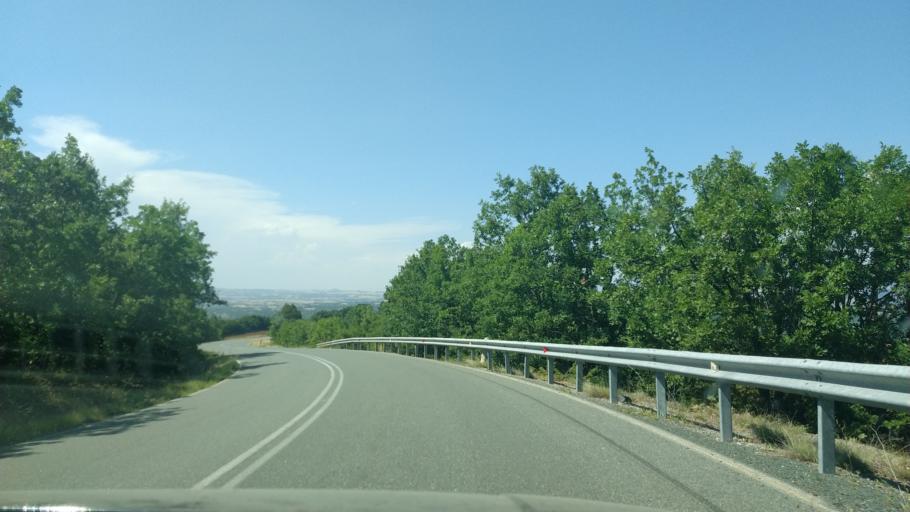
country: GR
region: West Macedonia
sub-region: Nomos Grevenon
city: Grevena
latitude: 40.0244
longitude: 21.4851
